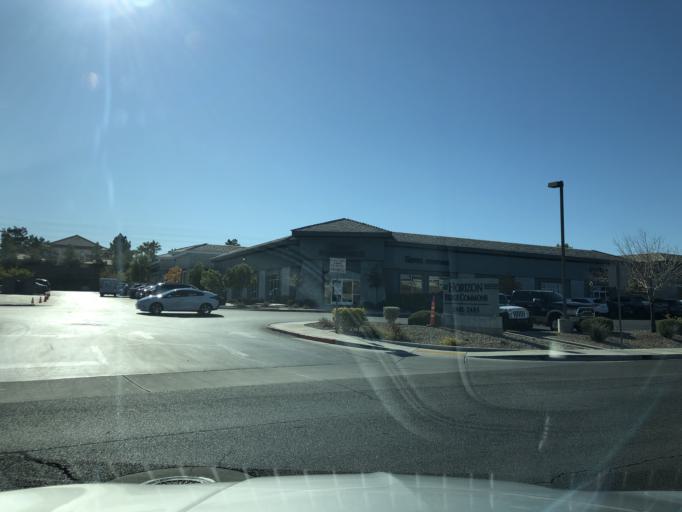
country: US
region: Nevada
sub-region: Clark County
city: Whitney
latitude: 36.0058
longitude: -115.0933
